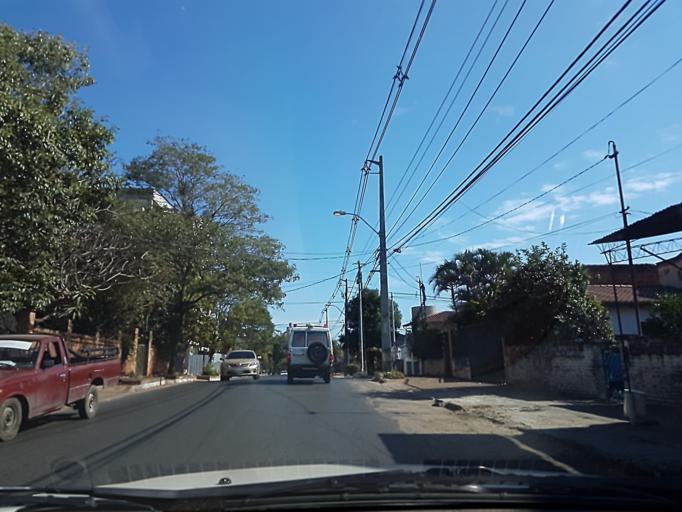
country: PY
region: Asuncion
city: Asuncion
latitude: -25.2790
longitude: -57.6028
